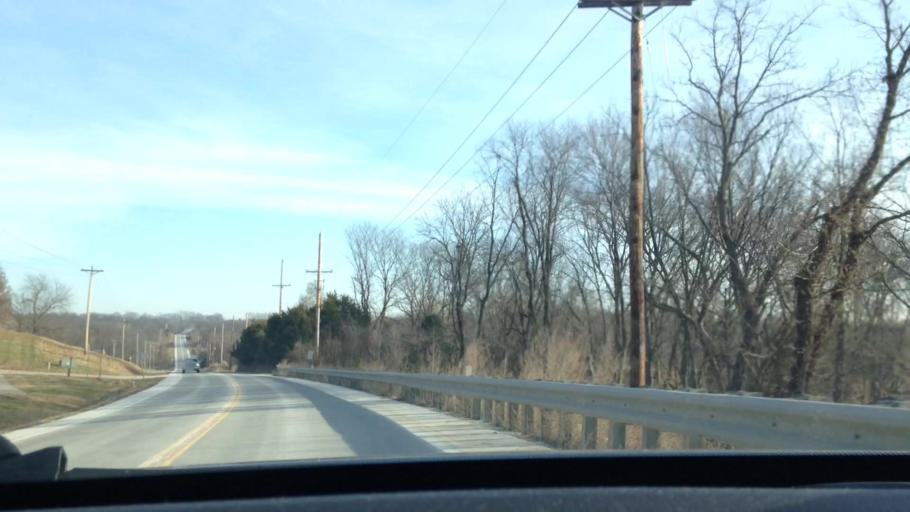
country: US
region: Missouri
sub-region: Platte County
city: Weston
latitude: 39.4146
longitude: -94.8872
